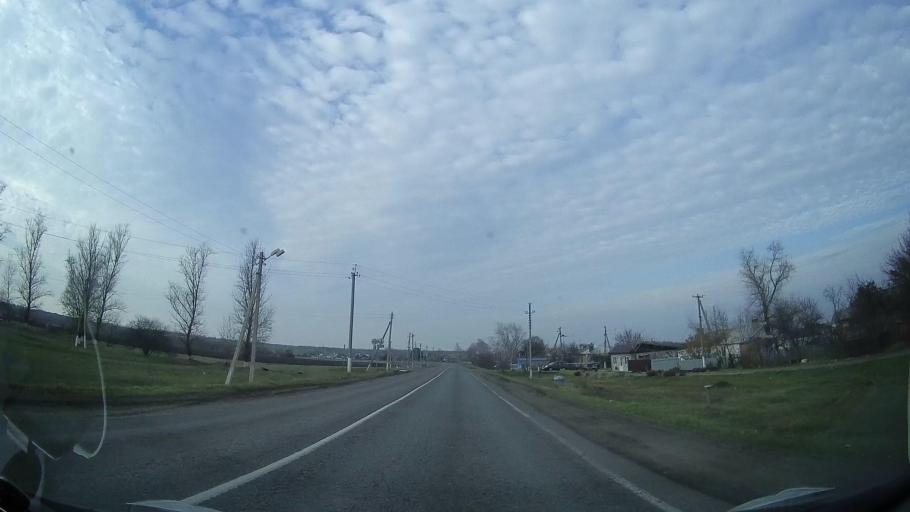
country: RU
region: Rostov
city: Bagayevskaya
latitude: 47.0935
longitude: 40.3153
